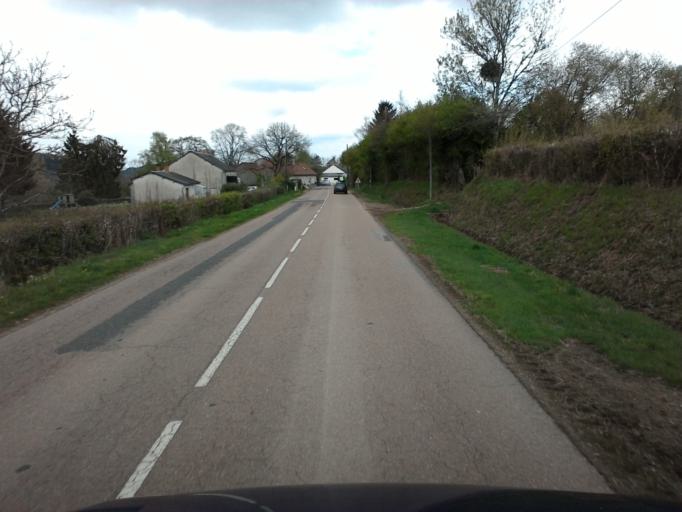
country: FR
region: Bourgogne
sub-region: Departement de la Cote-d'Or
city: Saulieu
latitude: 47.2675
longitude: 4.0290
